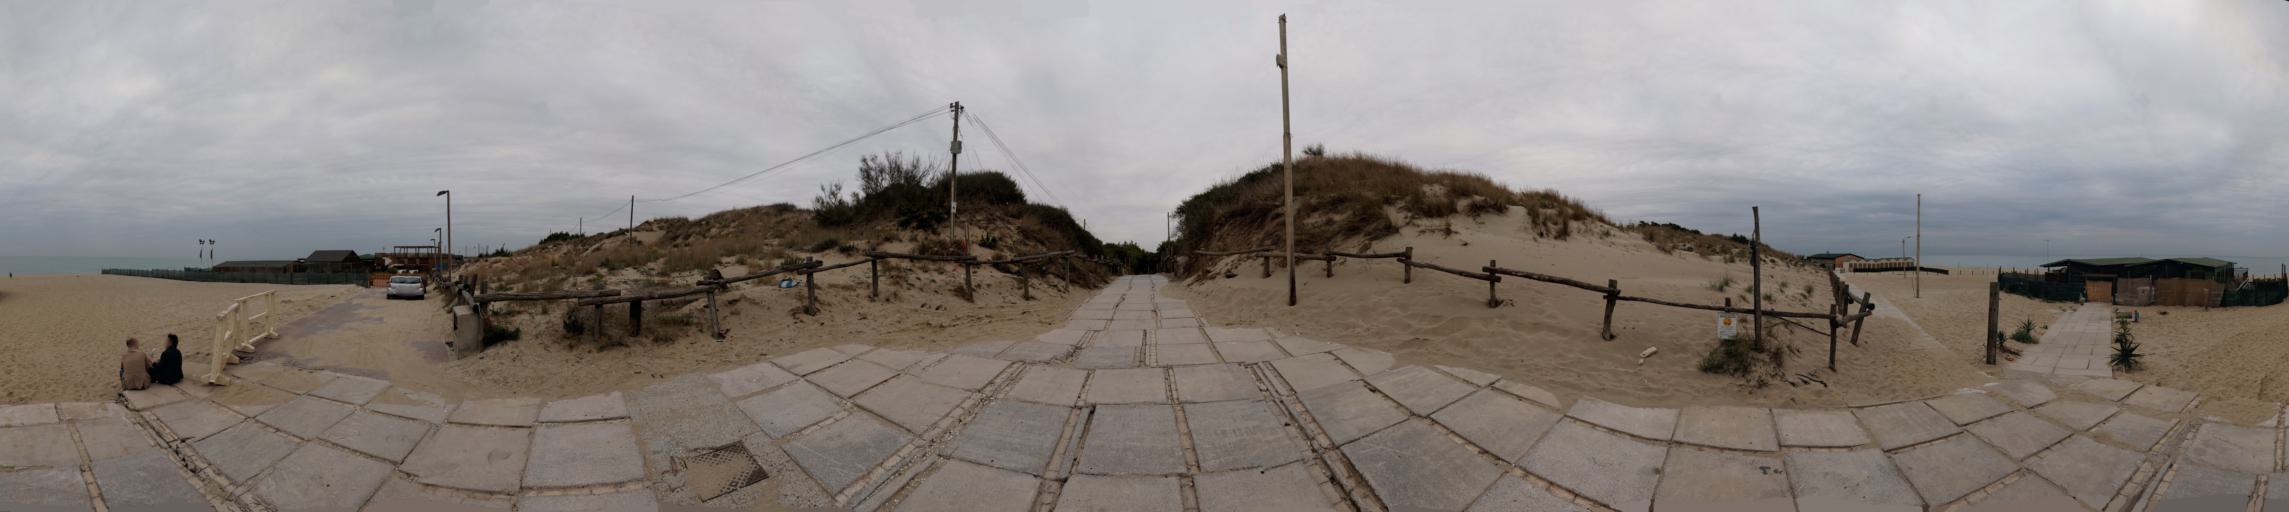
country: IT
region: Tuscany
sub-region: Province of Pisa
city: Marina di Pisa-Tirrenia-Calambrone
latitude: 43.6338
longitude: 10.2882
